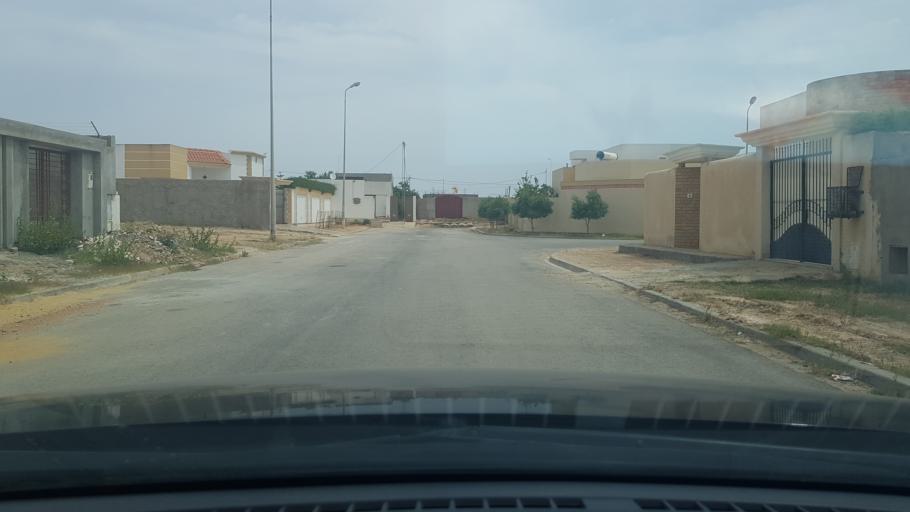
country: TN
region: Safaqis
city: Al Qarmadah
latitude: 34.8278
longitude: 10.7494
